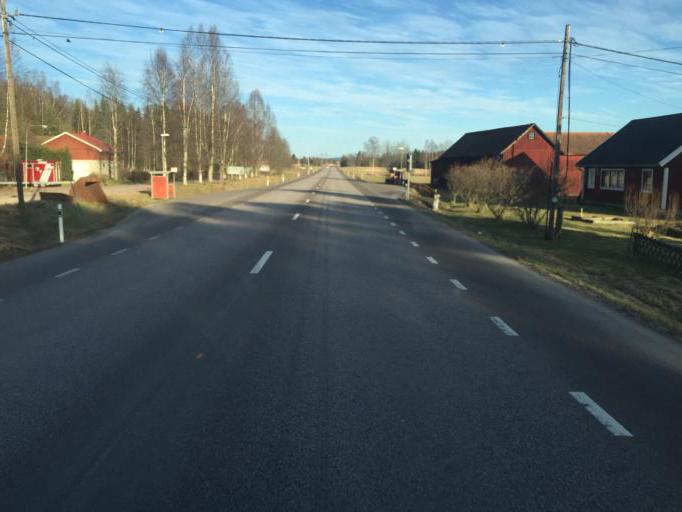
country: SE
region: Dalarna
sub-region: Gagnefs Kommun
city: Djuras
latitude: 60.5560
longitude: 15.1462
